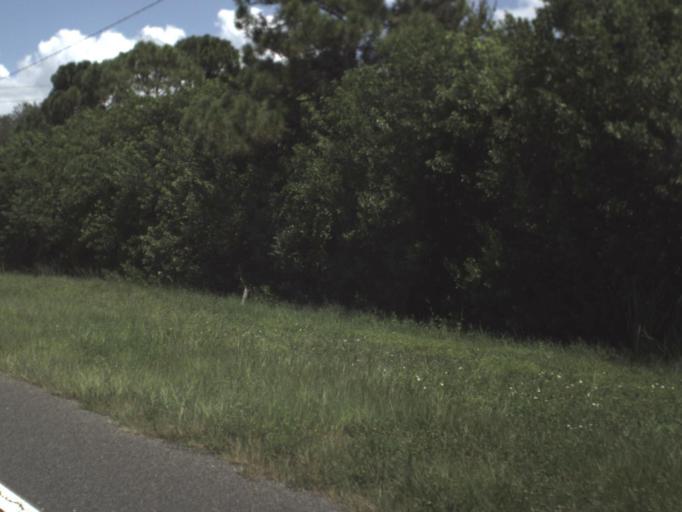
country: US
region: Florida
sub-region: Pinellas County
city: Gandy
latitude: 27.8752
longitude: -82.6387
